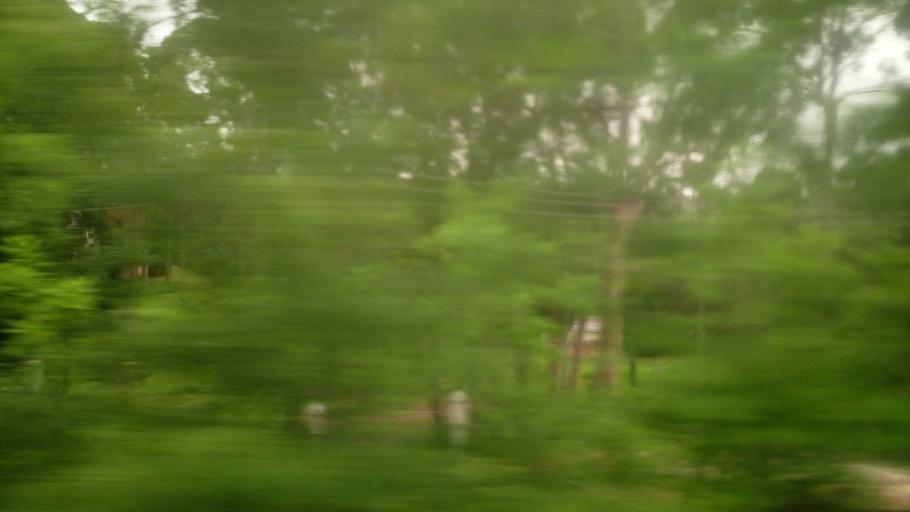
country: AU
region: New South Wales
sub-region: Blue Mountains Municipality
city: Blaxland
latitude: -33.7028
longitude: 150.5749
